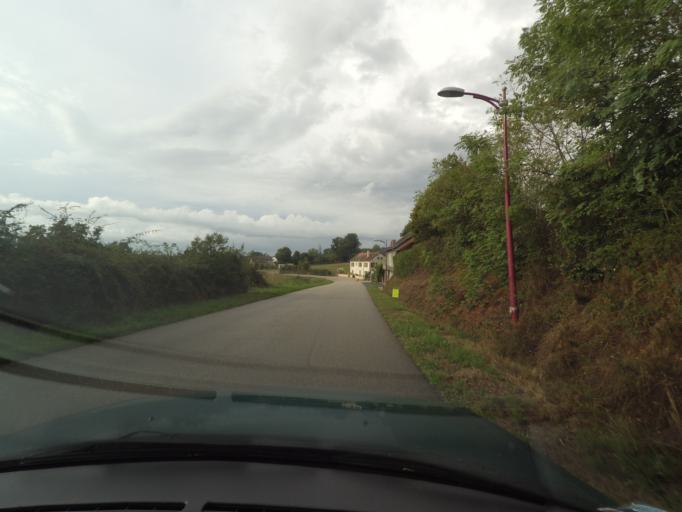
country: FR
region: Limousin
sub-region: Departement de la Haute-Vienne
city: Nexon
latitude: 45.7114
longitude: 1.1576
